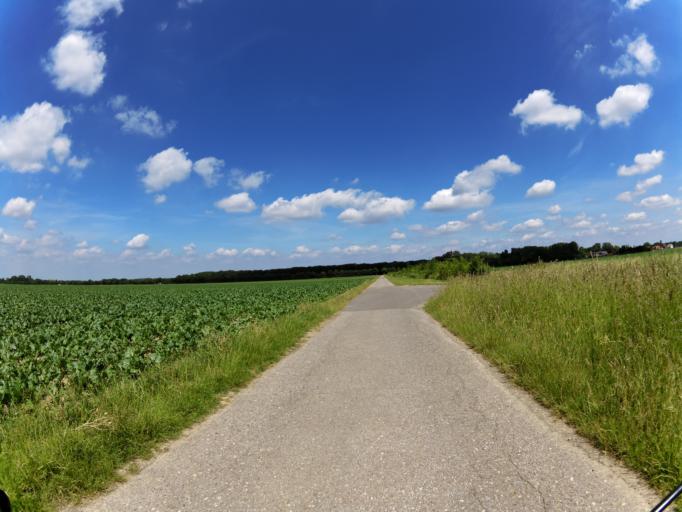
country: DE
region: North Rhine-Westphalia
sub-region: Regierungsbezirk Koln
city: Selfkant
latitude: 51.0296
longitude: 5.8976
